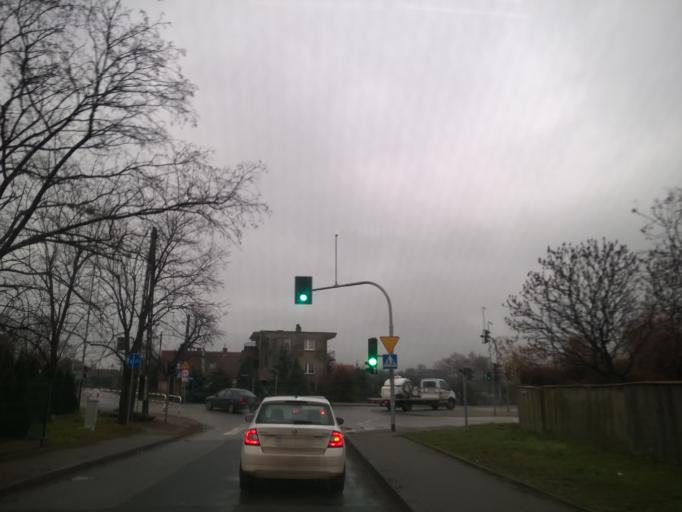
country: PL
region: Lower Silesian Voivodeship
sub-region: Powiat trzebnicki
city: Psary
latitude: 51.2077
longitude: 17.0388
